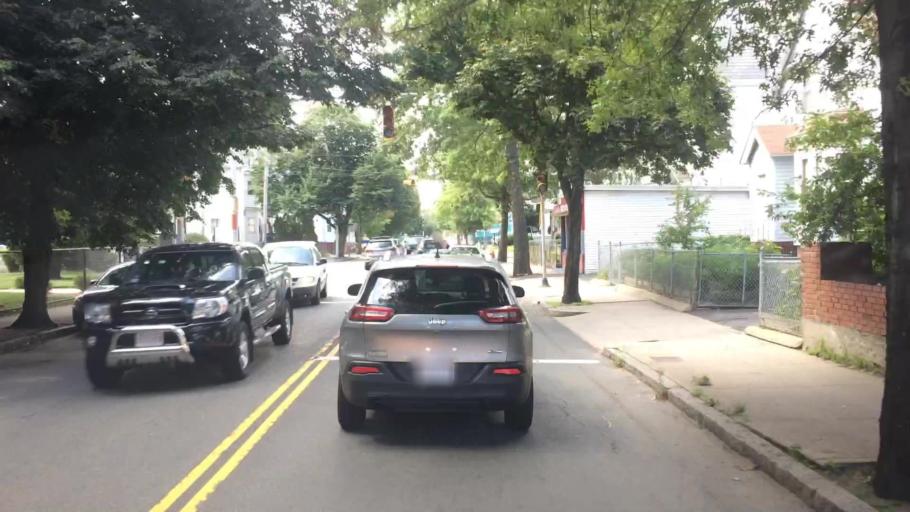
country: US
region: Massachusetts
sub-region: Essex County
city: Lynn
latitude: 42.4676
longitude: -70.9531
